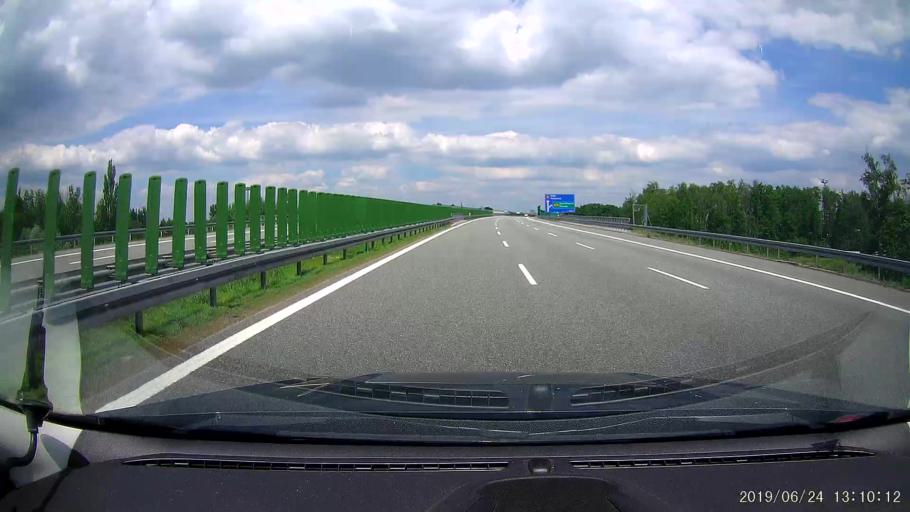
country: PL
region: Silesian Voivodeship
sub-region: Powiat gliwicki
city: Knurow
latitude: 50.2141
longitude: 18.6922
